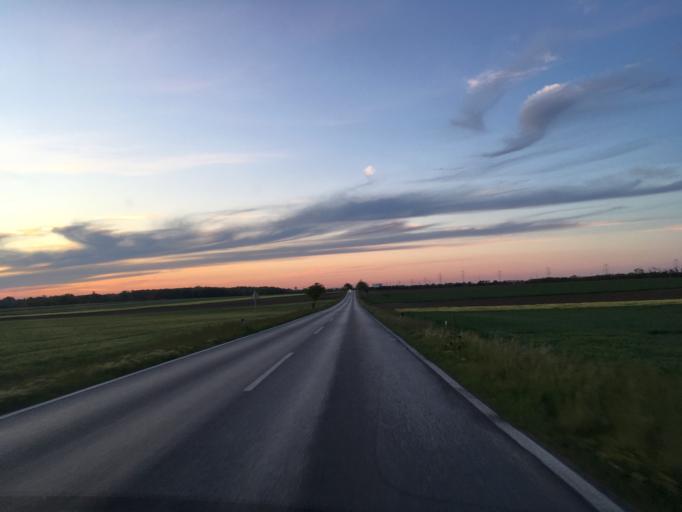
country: AT
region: Lower Austria
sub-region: Politischer Bezirk Wien-Umgebung
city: Moosbrunn
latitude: 48.0438
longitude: 16.4637
